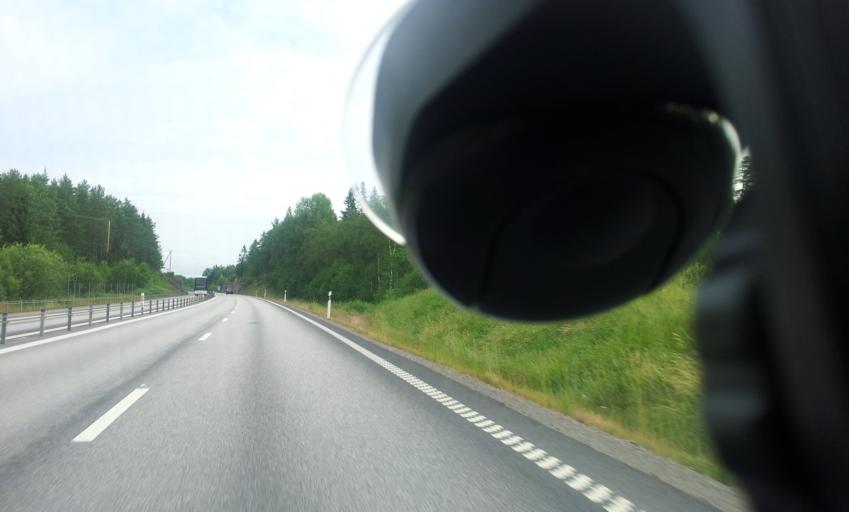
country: SE
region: OEstergoetland
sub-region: Valdemarsviks Kommun
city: Gusum
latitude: 58.2610
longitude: 16.5244
